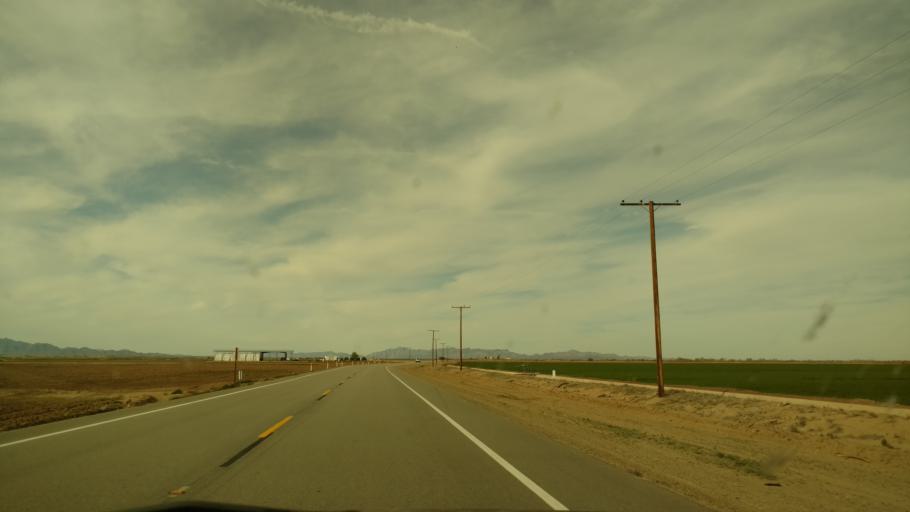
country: US
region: California
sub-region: Riverside County
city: Mesa Verde
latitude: 33.4478
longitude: -114.7317
